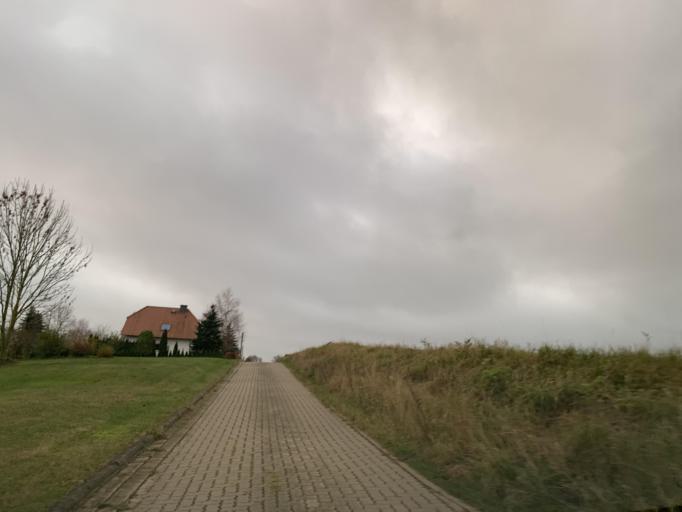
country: DE
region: Mecklenburg-Vorpommern
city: Blankensee
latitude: 53.3945
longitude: 13.3085
